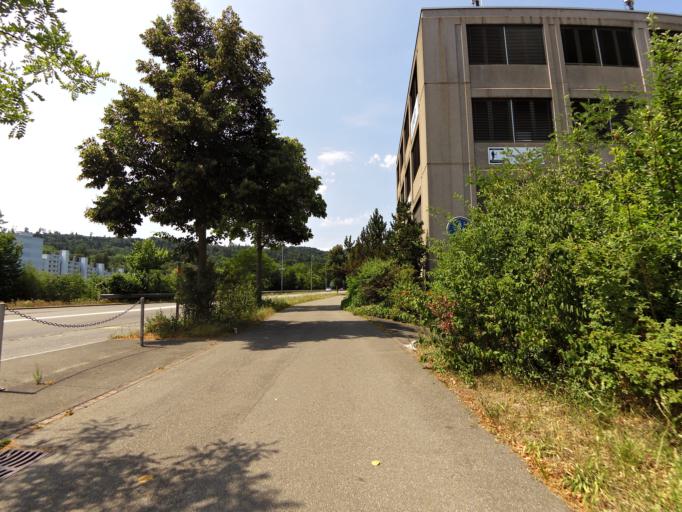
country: CH
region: Aargau
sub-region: Bezirk Baden
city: Wettingen
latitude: 47.4593
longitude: 8.3152
